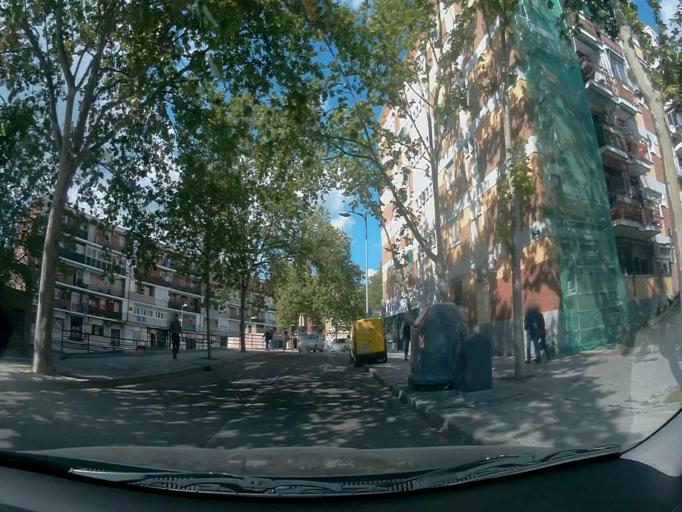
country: ES
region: Madrid
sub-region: Provincia de Madrid
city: Alcorcon
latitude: 40.3468
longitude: -3.8332
